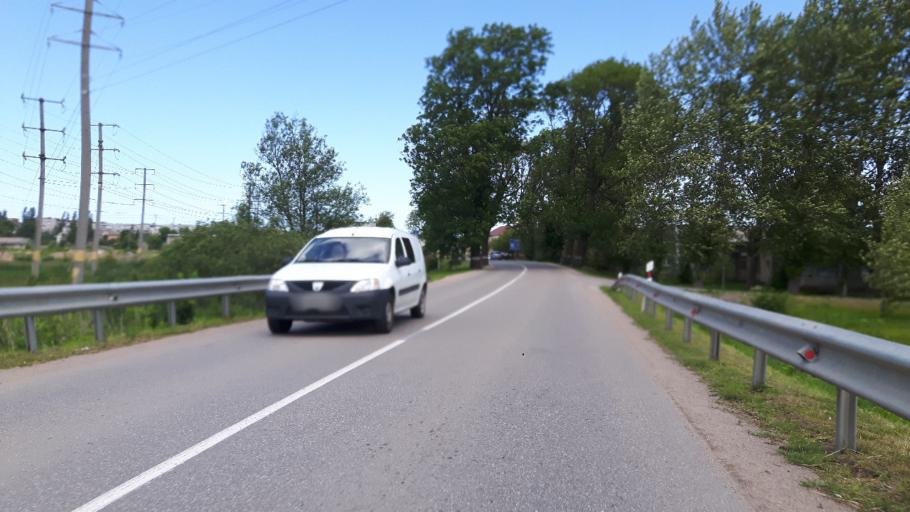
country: RU
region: Kaliningrad
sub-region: Zelenogradskiy Rayon
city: Zelenogradsk
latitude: 54.9483
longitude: 20.4694
